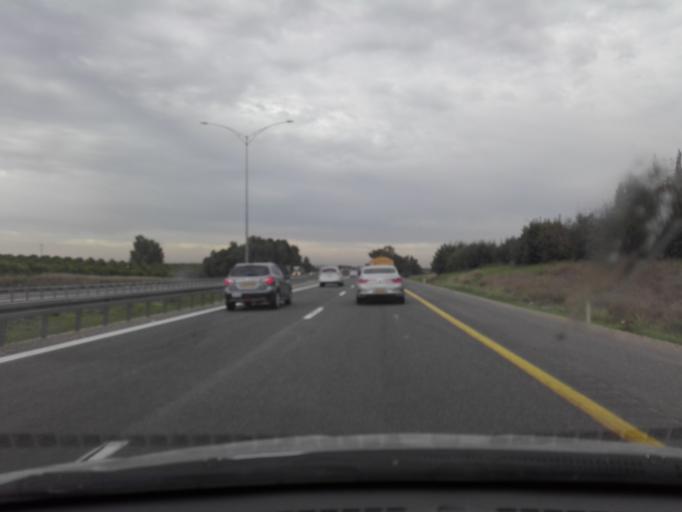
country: IL
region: Central District
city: Mazkeret Batya
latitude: 31.8759
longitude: 34.8763
